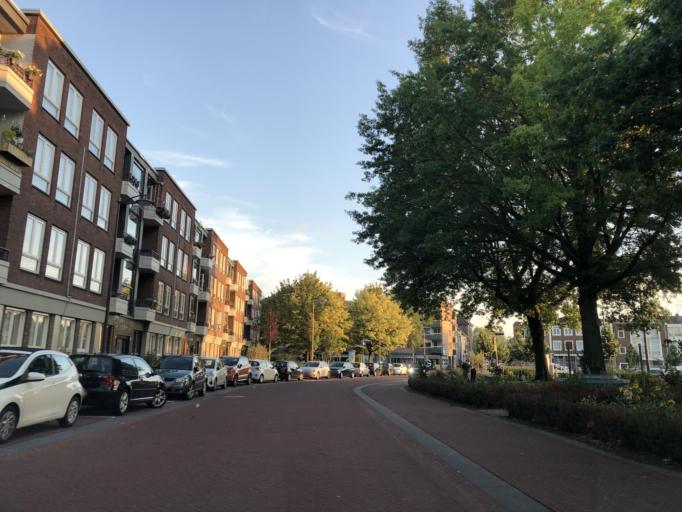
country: NL
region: Gelderland
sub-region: Gemeente Arnhem
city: Arnhem
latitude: 51.9788
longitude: 5.9084
